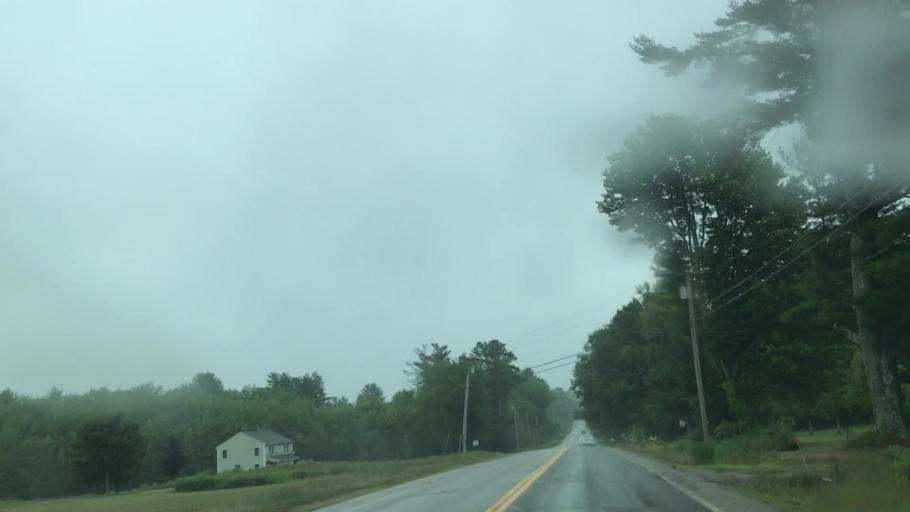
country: US
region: Maine
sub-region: York County
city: North Berwick
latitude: 43.2989
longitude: -70.7752
